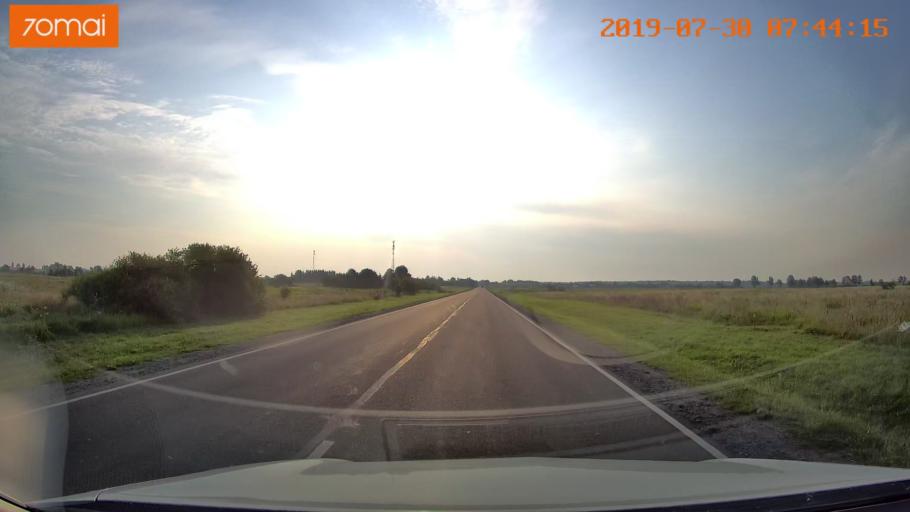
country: RU
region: Kaliningrad
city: Gvardeysk
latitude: 54.6498
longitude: 21.3203
